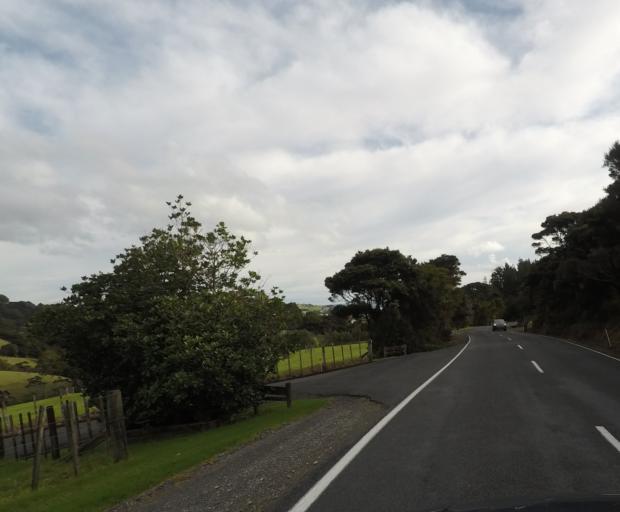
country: NZ
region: Northland
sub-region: Whangarei
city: Ruakaka
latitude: -36.0537
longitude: 174.5473
